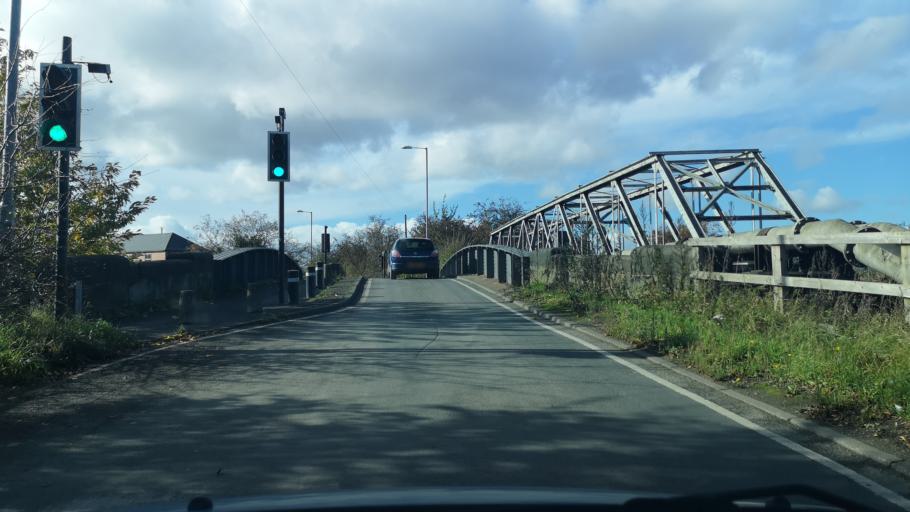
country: GB
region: England
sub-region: City and Borough of Wakefield
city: Wakefield
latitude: 53.7040
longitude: -1.4615
